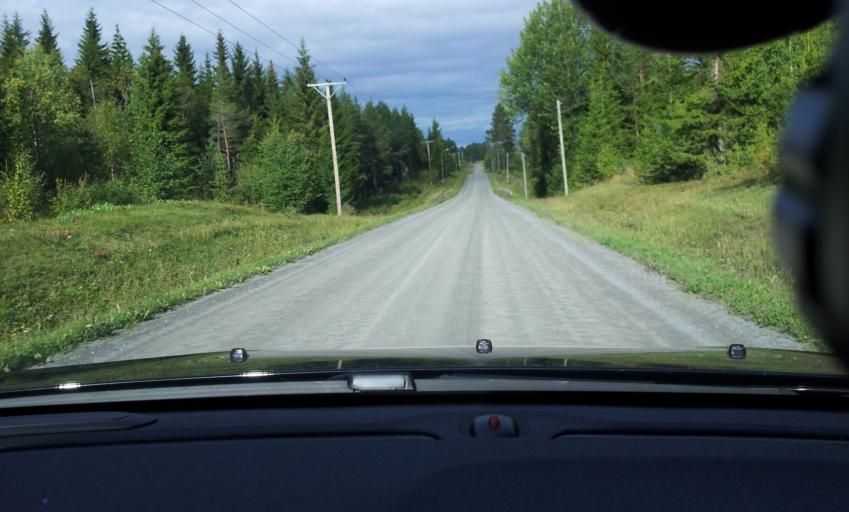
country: SE
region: Jaemtland
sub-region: Krokoms Kommun
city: Valla
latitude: 63.2504
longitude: 13.9566
